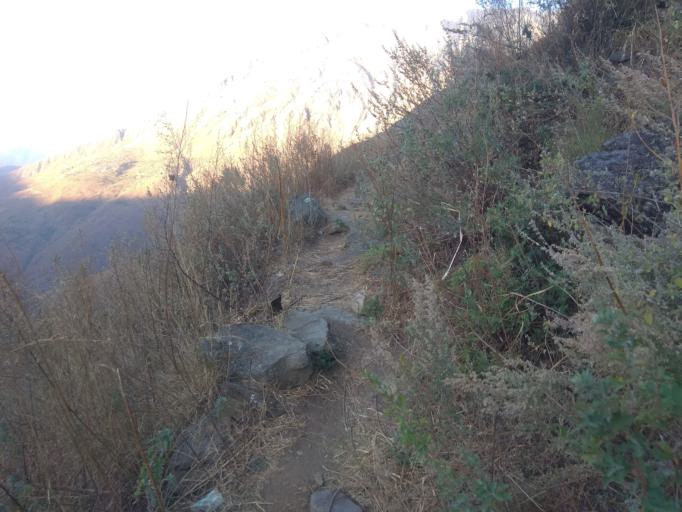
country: NP
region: Mid Western
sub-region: Bheri Zone
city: Dailekh
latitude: 29.2860
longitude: 81.7157
